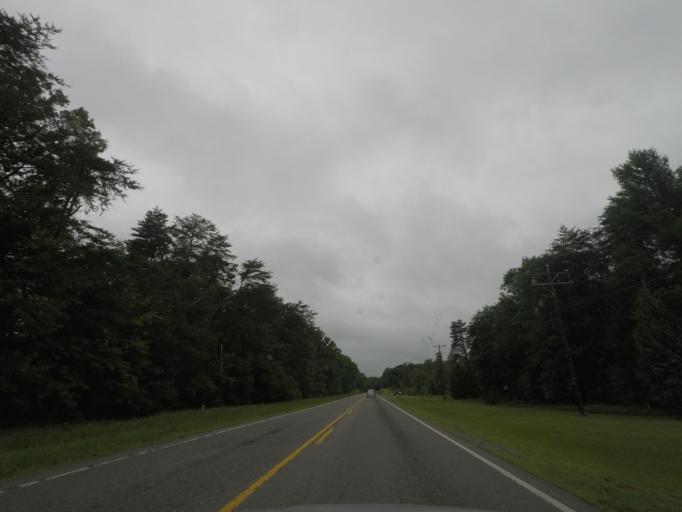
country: US
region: Virginia
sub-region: Fluvanna County
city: Palmyra
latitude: 37.8171
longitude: -78.2604
